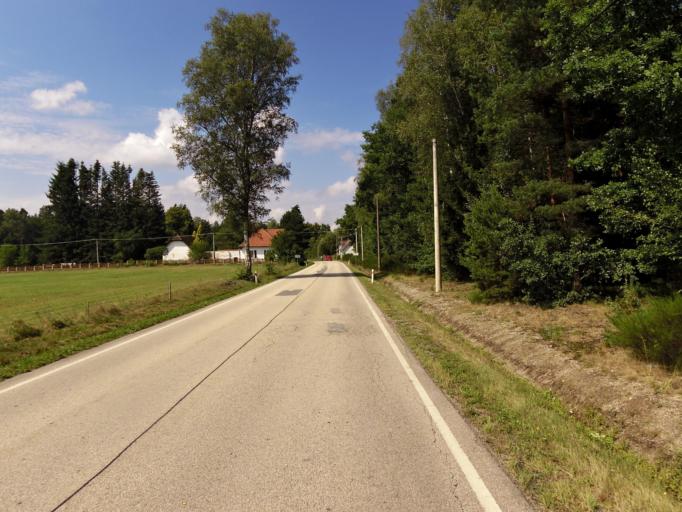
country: CZ
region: Jihocesky
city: Chlum u Trebone
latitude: 48.9500
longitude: 14.8927
